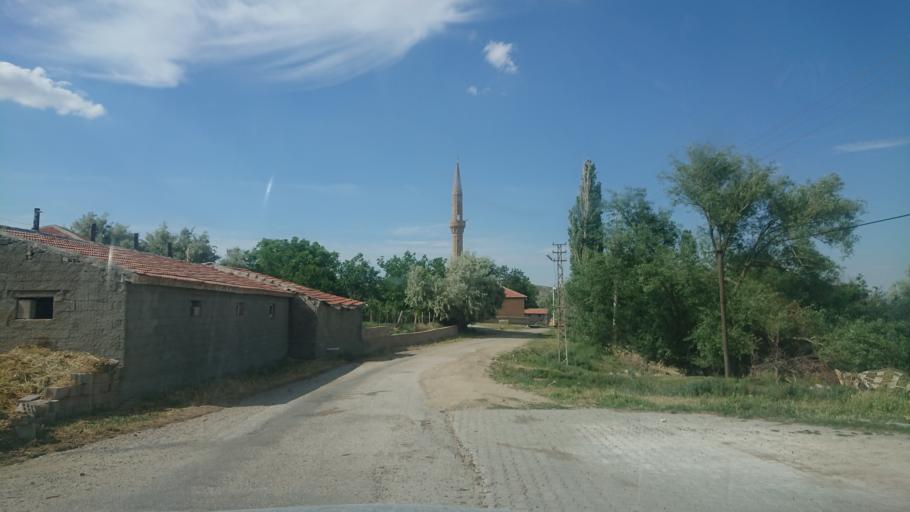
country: TR
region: Aksaray
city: Ortakoy
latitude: 38.8216
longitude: 34.0046
